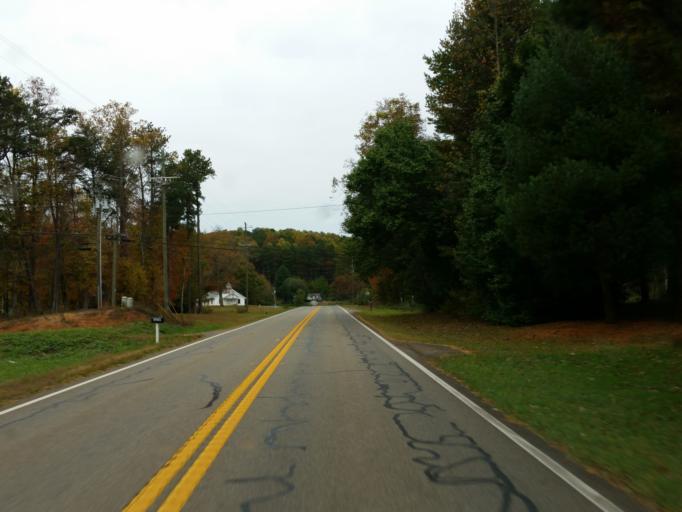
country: US
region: Georgia
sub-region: Pickens County
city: Jasper
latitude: 34.5237
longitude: -84.4173
